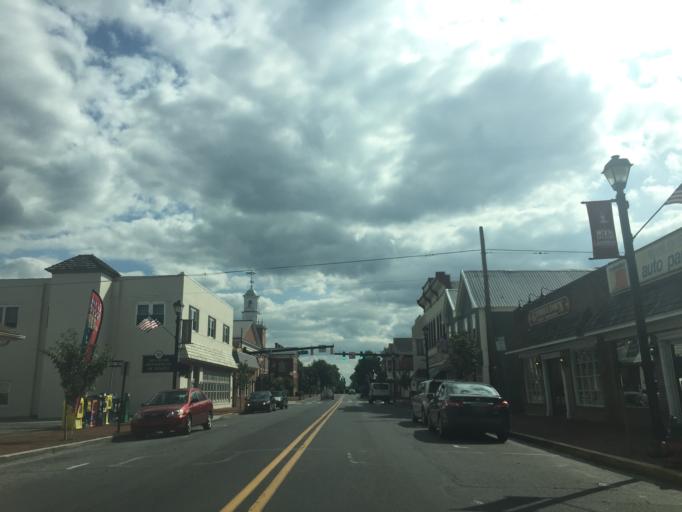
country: US
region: Delaware
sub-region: Sussex County
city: Georgetown
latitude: 38.6915
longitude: -75.3841
